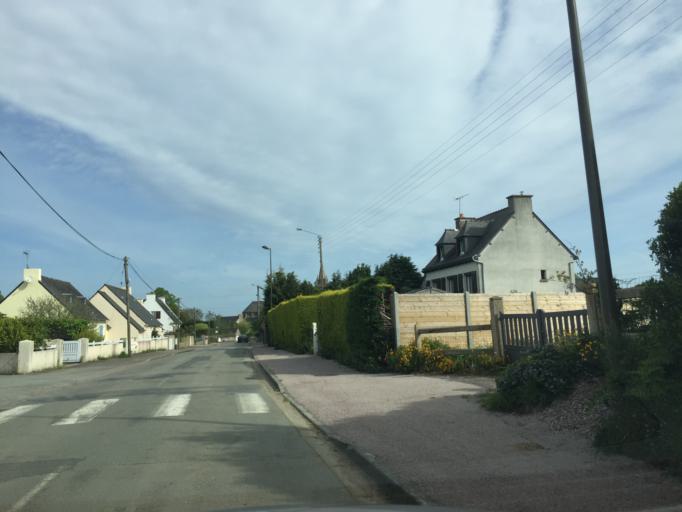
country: FR
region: Brittany
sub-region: Departement des Cotes-d'Armor
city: Matignon
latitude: 48.6523
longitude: -2.3313
